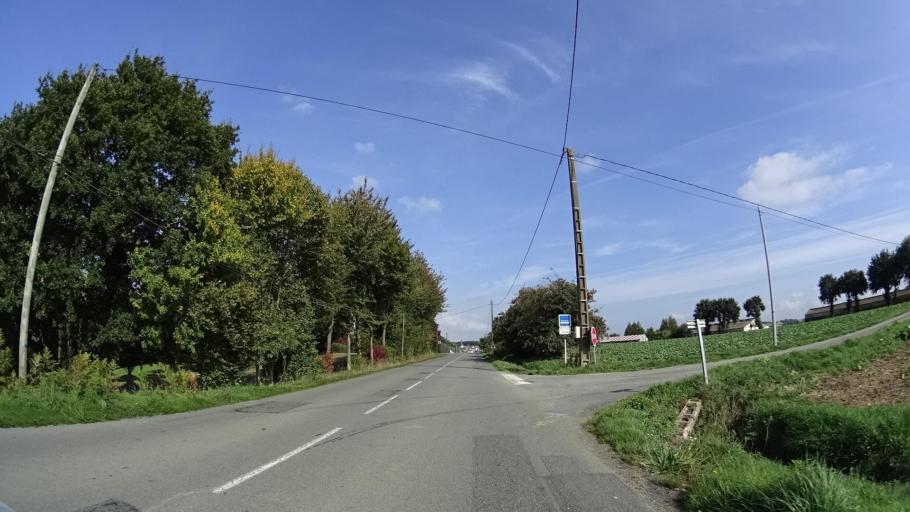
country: FR
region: Brittany
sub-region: Departement d'Ille-et-Vilaine
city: Quedillac
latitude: 48.2428
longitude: -2.1512
